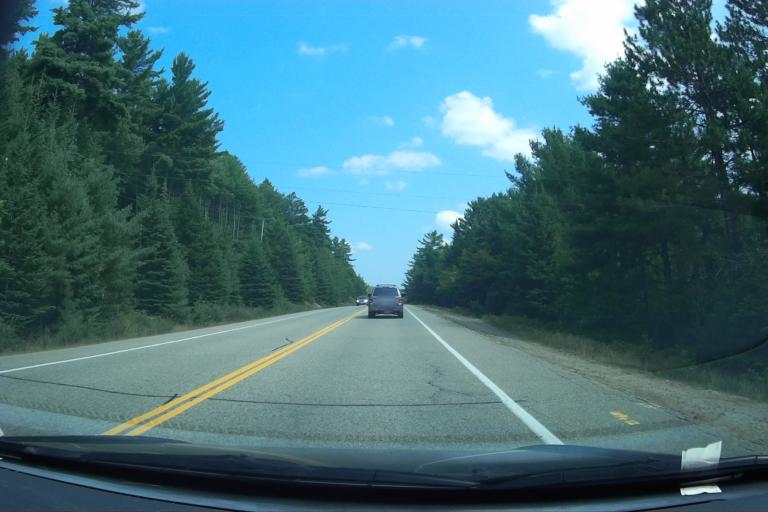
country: CA
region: Ontario
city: Huntsville
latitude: 45.5805
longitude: -78.4999
